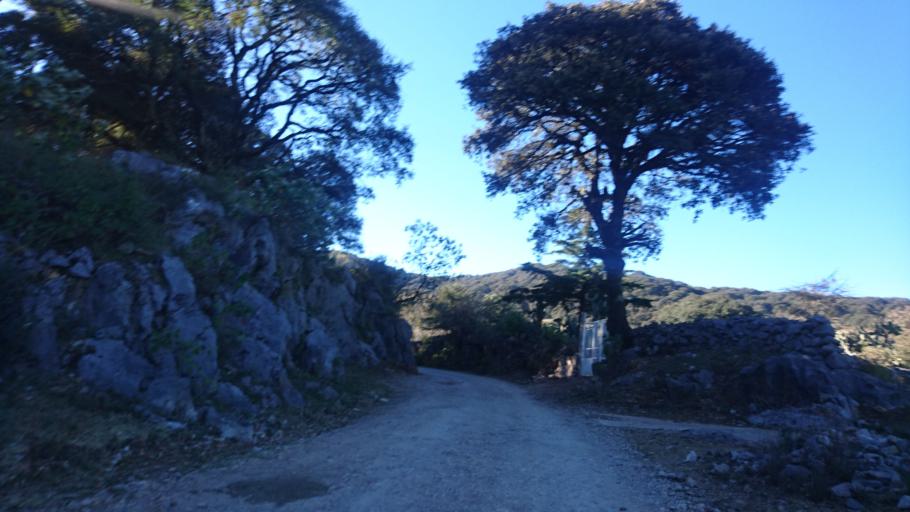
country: MX
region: San Luis Potosi
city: Zaragoza
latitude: 22.0310
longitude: -100.6094
